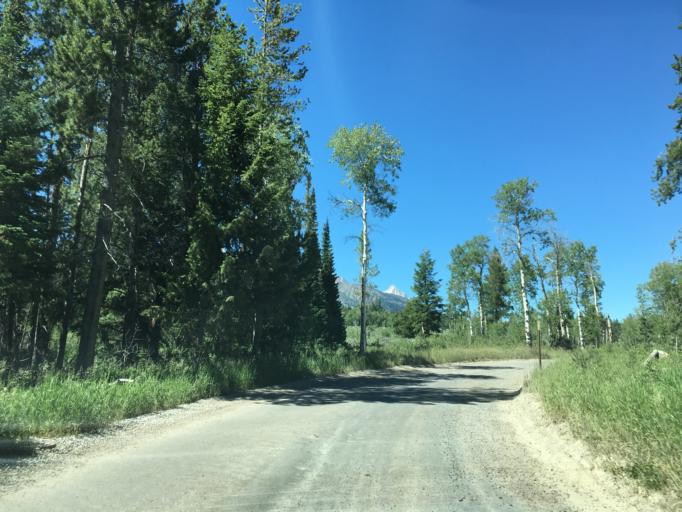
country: US
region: Wyoming
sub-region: Teton County
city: Moose Wilson Road
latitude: 43.6058
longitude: -110.7934
